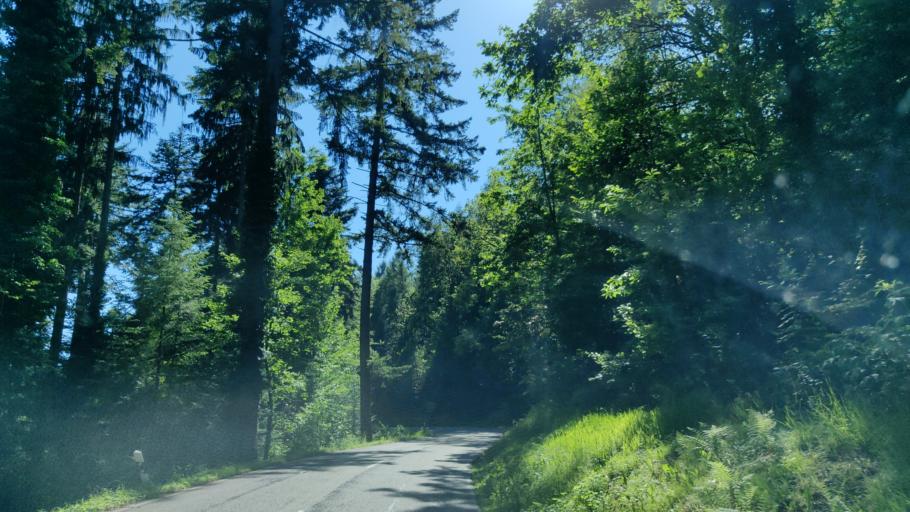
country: DE
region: Baden-Wuerttemberg
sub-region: Karlsruhe Region
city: Gernsbach
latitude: 48.7540
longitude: 8.3126
